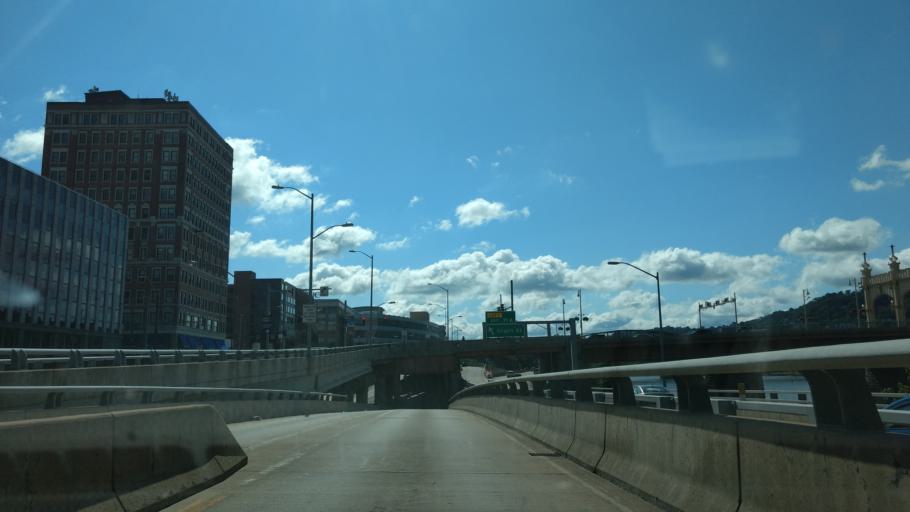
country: US
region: Pennsylvania
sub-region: Allegheny County
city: Pittsburgh
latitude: 40.4370
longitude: -80.0026
